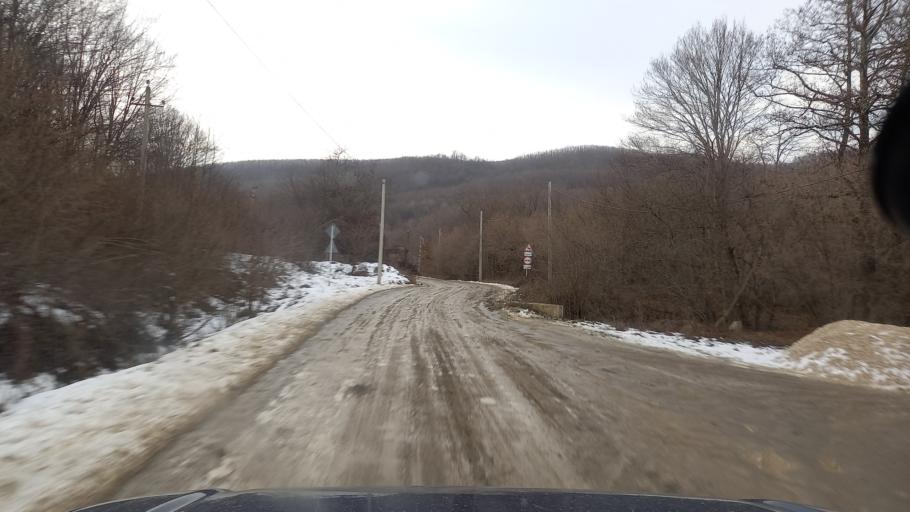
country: RU
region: Adygeya
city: Kamennomostskiy
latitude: 44.1412
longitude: 40.2803
